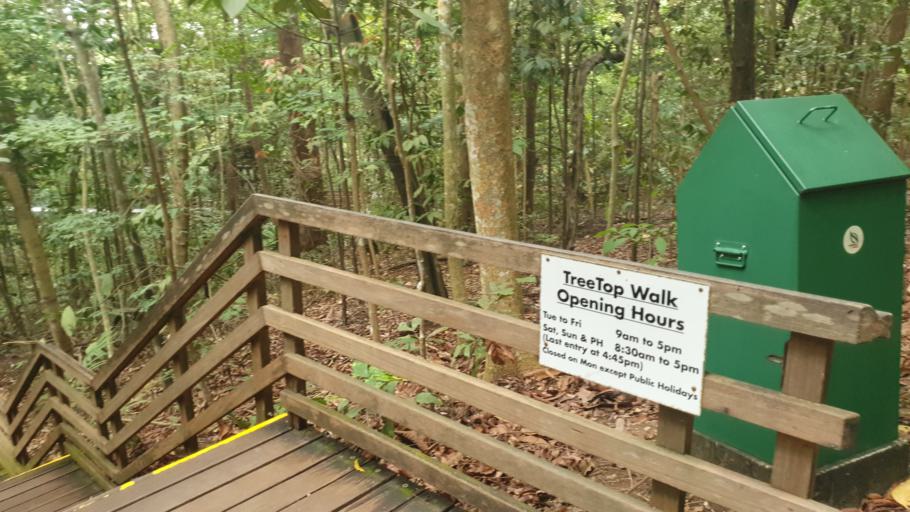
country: SG
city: Singapore
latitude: 1.3604
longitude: 103.8126
